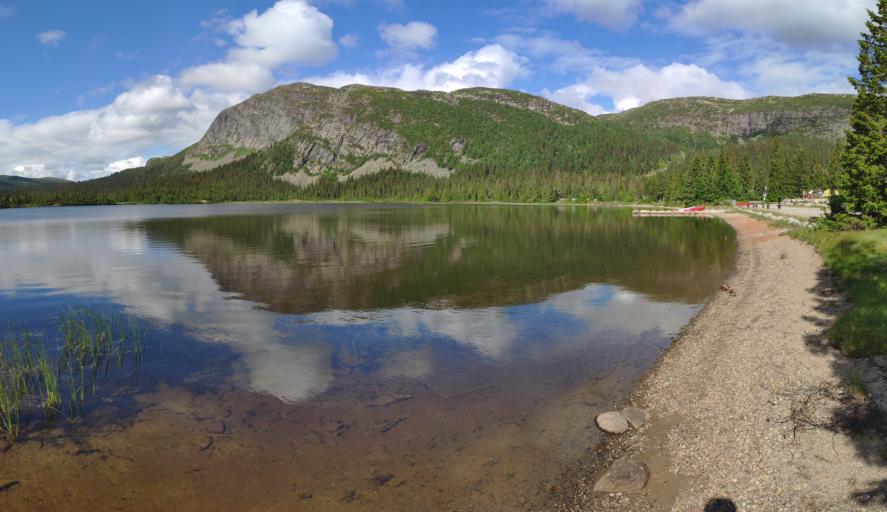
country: NO
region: Buskerud
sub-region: Nes
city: Nesbyen
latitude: 60.3398
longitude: 9.1846
